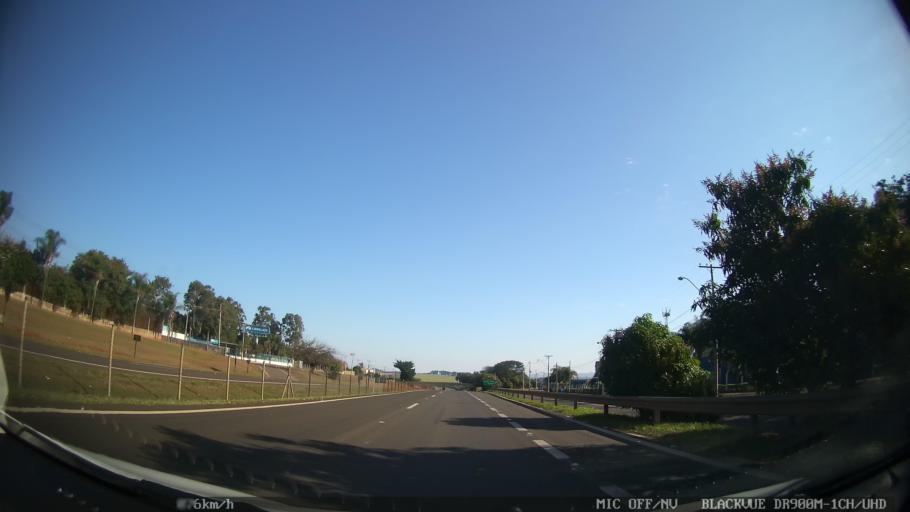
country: BR
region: Sao Paulo
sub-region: Piracicaba
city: Piracicaba
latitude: -22.6718
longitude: -47.6280
